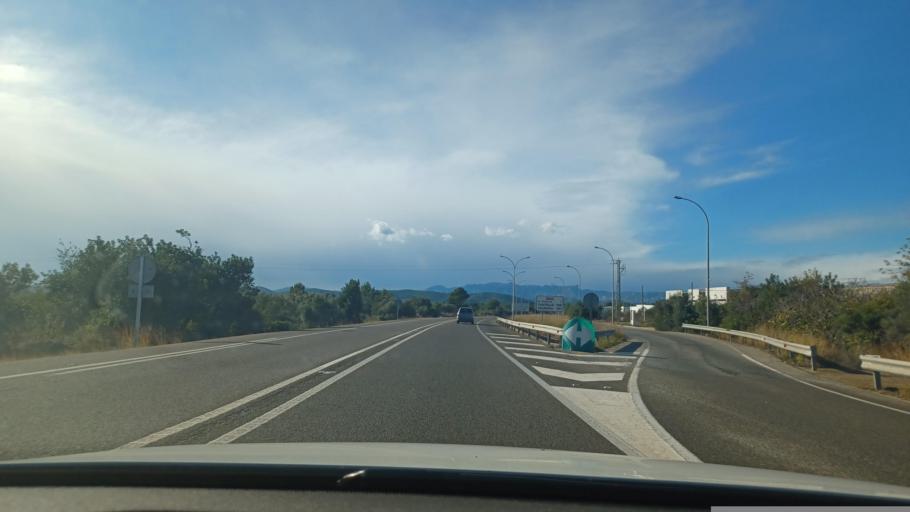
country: ES
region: Catalonia
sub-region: Provincia de Tarragona
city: l'Ametlla de Mar
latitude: 40.8933
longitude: 0.7848
